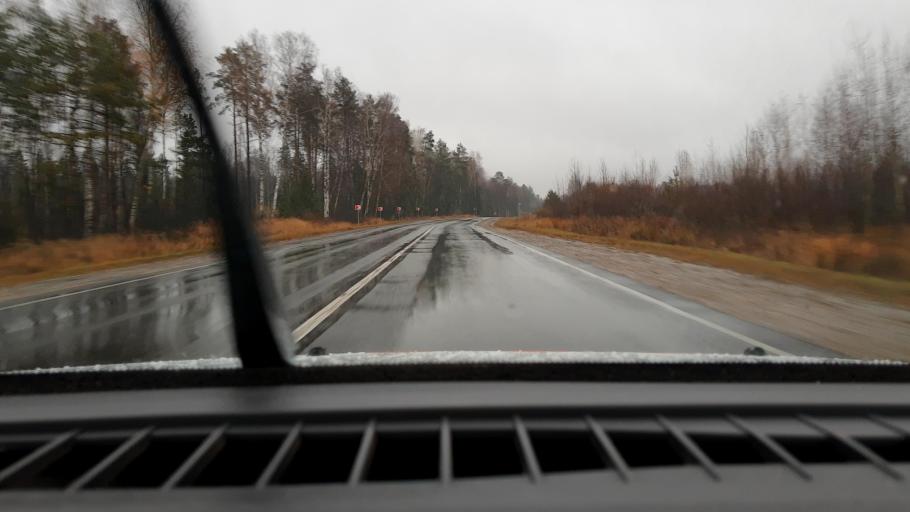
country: RU
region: Nizjnij Novgorod
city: Linda
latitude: 56.6317
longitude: 44.0929
